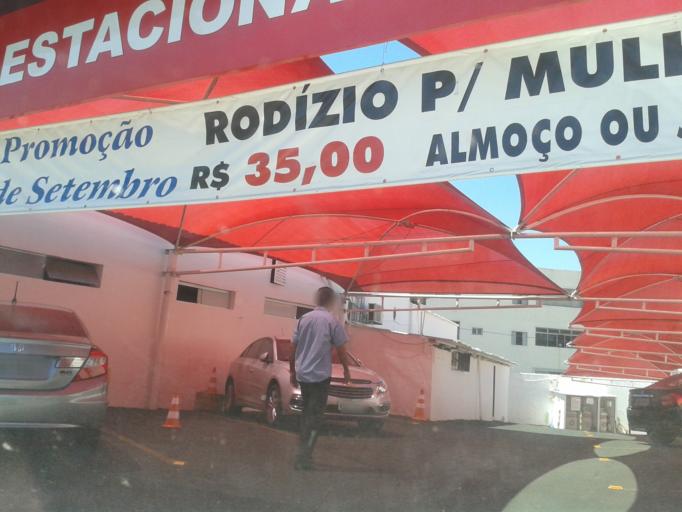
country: BR
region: Minas Gerais
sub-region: Uberlandia
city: Uberlandia
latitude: -18.9137
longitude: -48.2670
